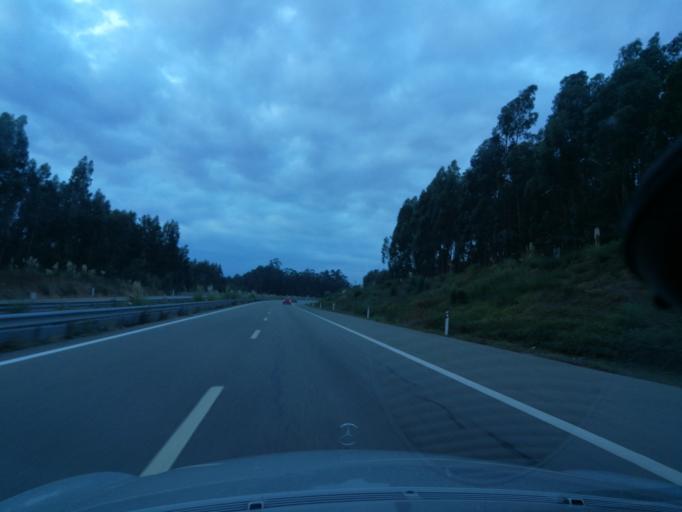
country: PT
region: Aveiro
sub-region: Estarreja
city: Beduido
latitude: 40.7704
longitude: -8.5569
